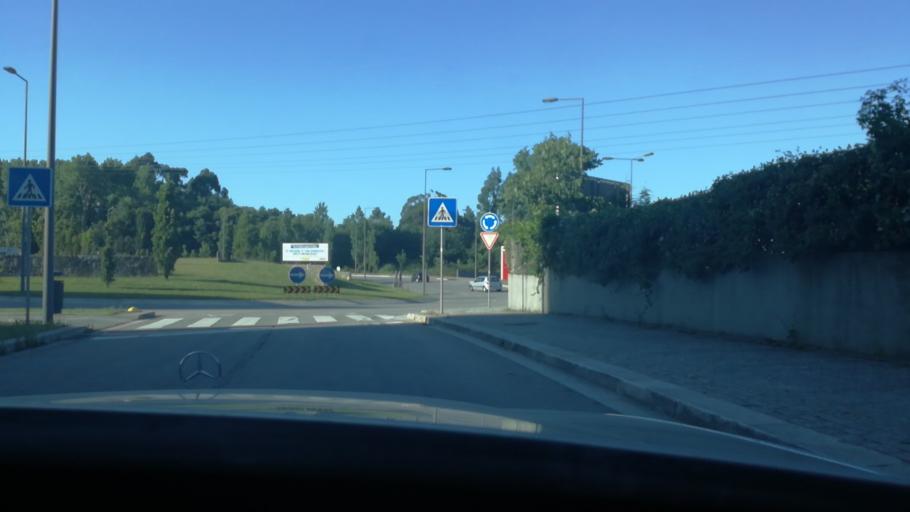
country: PT
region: Porto
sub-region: Maia
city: Nogueira
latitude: 41.2361
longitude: -8.5995
